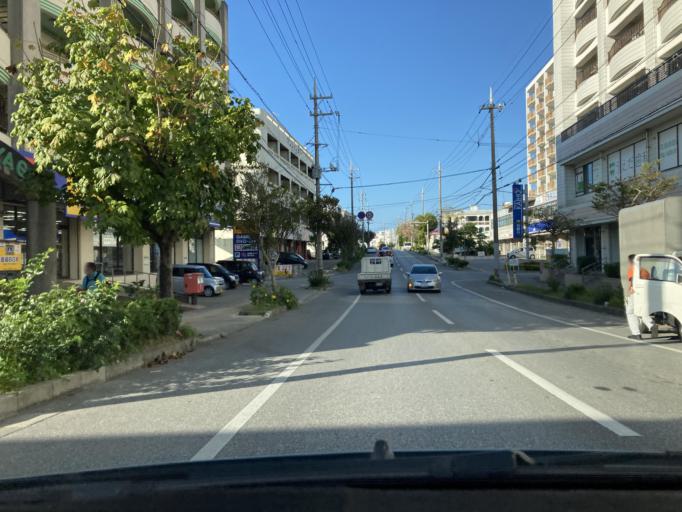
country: JP
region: Okinawa
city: Ginowan
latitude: 26.2524
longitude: 127.7139
